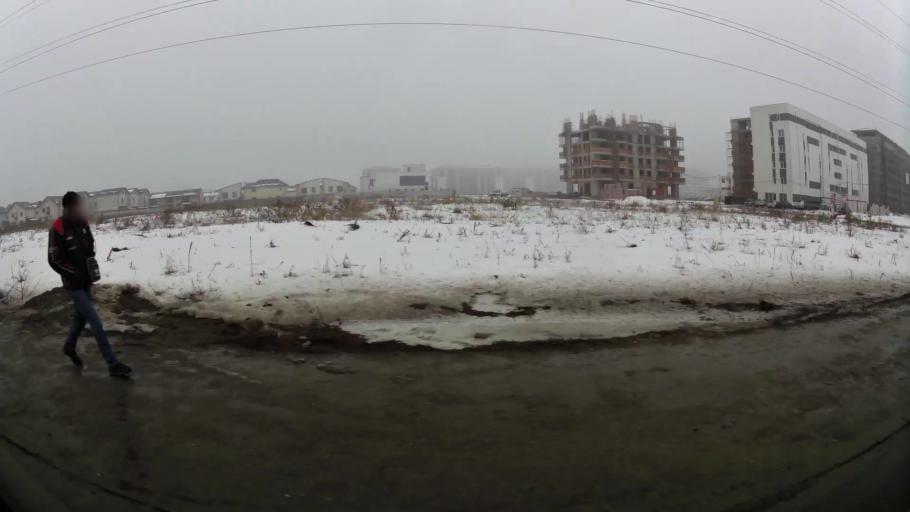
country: RO
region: Ilfov
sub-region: Comuna Chiajna
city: Rosu
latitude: 44.4480
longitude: 25.9931
